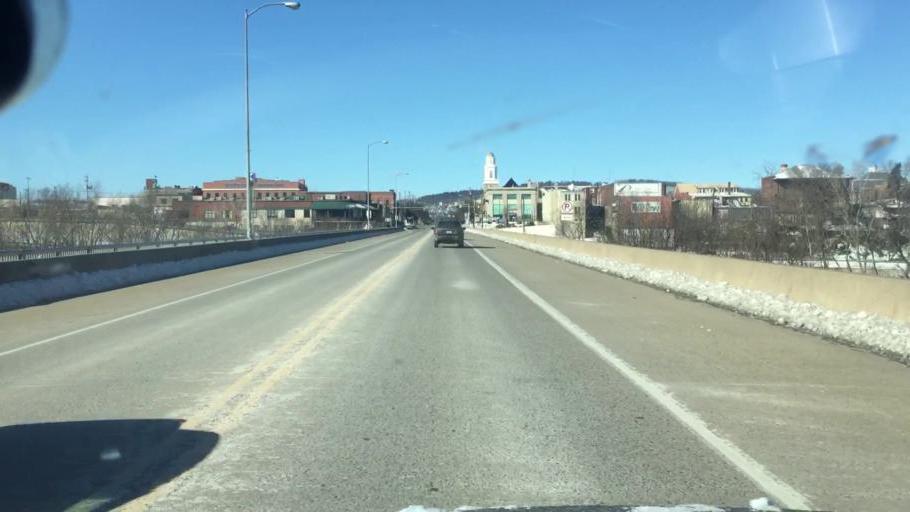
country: US
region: Pennsylvania
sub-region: Columbia County
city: Berwick
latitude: 41.0526
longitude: -76.2318
